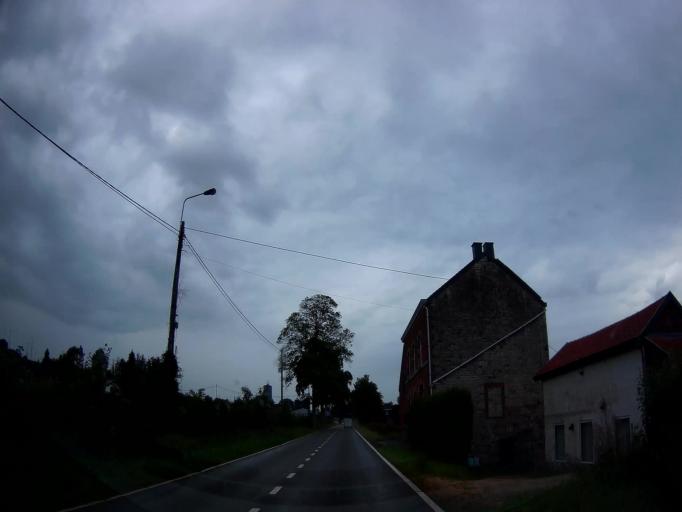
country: BE
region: Wallonia
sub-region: Province de Liege
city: Aywaille
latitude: 50.5050
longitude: 5.7277
